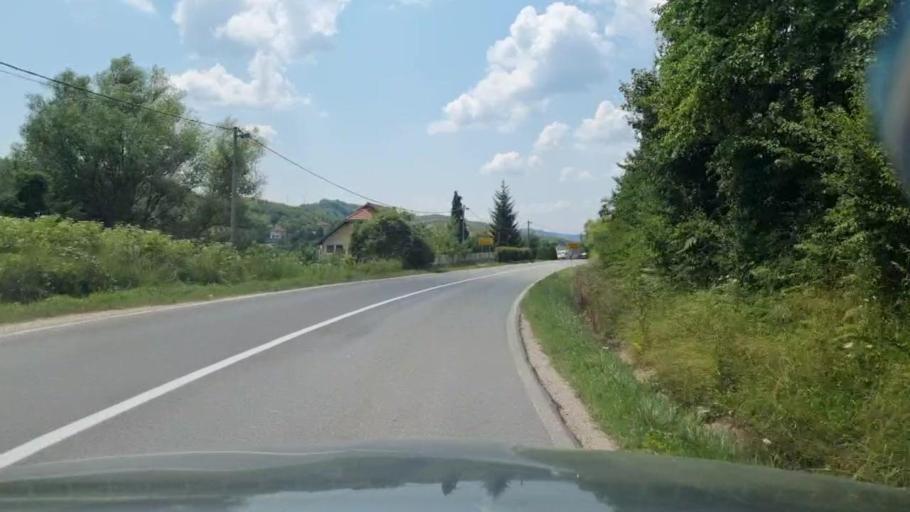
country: BA
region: Federation of Bosnia and Herzegovina
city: Gornja Tuzla
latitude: 44.5311
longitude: 18.7741
